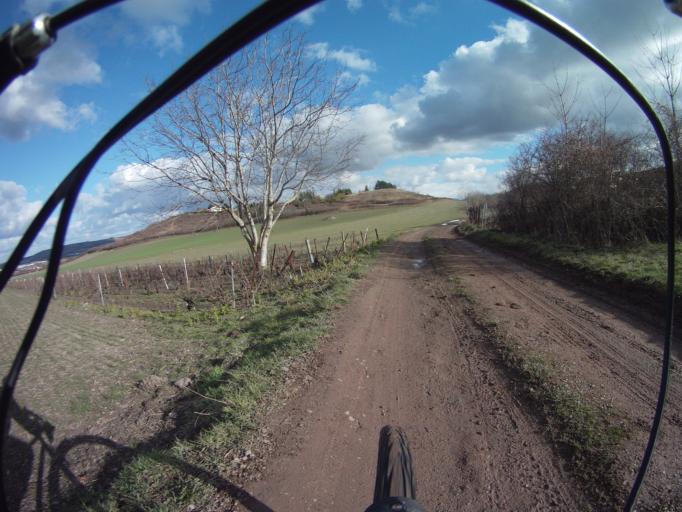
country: FR
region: Auvergne
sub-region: Departement du Puy-de-Dome
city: Perignat-les-Sarlieve
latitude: 45.7383
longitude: 3.1286
